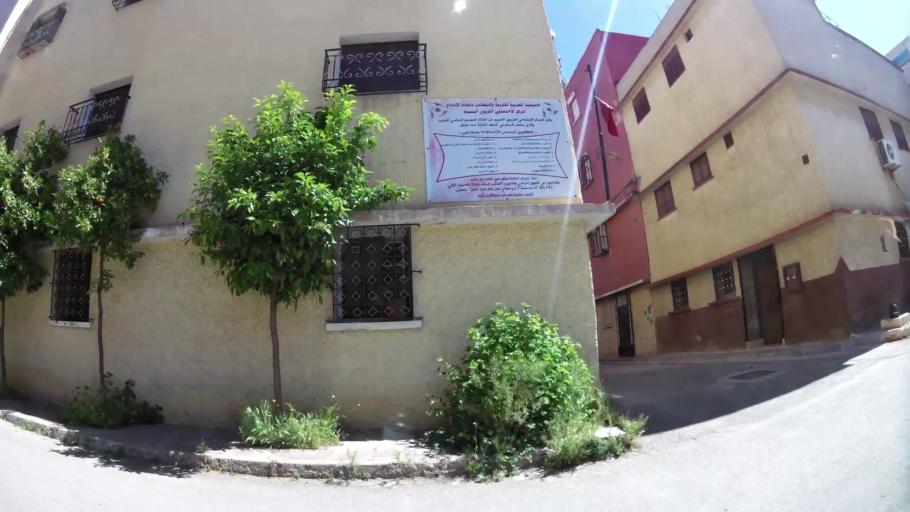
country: MA
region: Meknes-Tafilalet
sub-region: Meknes
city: Meknes
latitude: 33.9057
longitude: -5.5263
